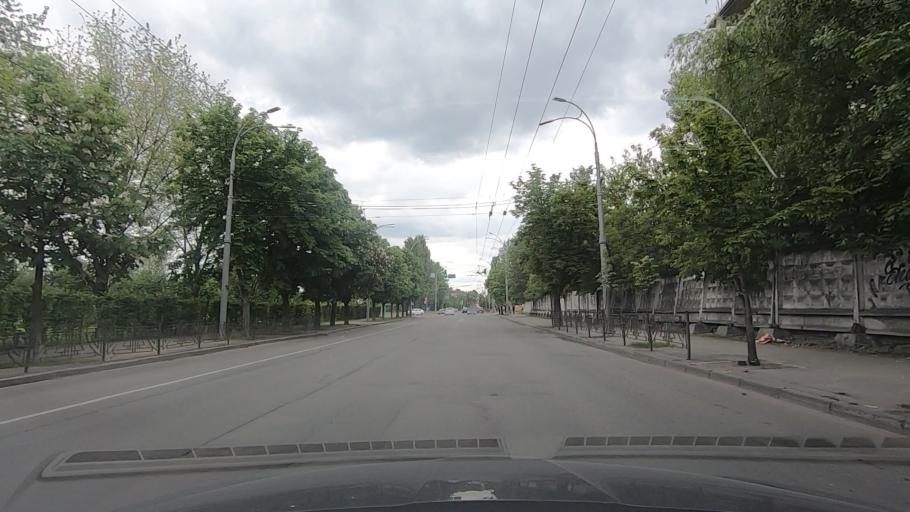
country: MD
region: Riscani
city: Riscani
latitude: 48.0520
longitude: 27.5898
